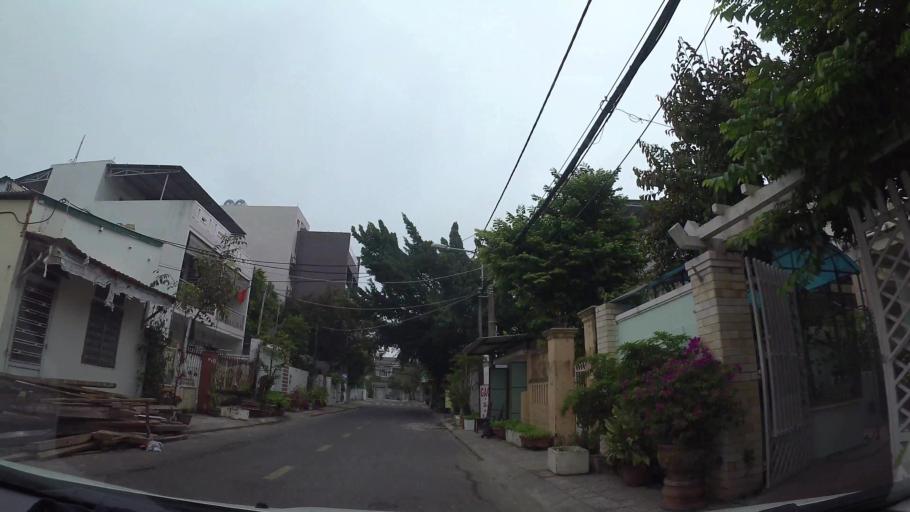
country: VN
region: Da Nang
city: Son Tra
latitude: 16.0416
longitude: 108.2466
